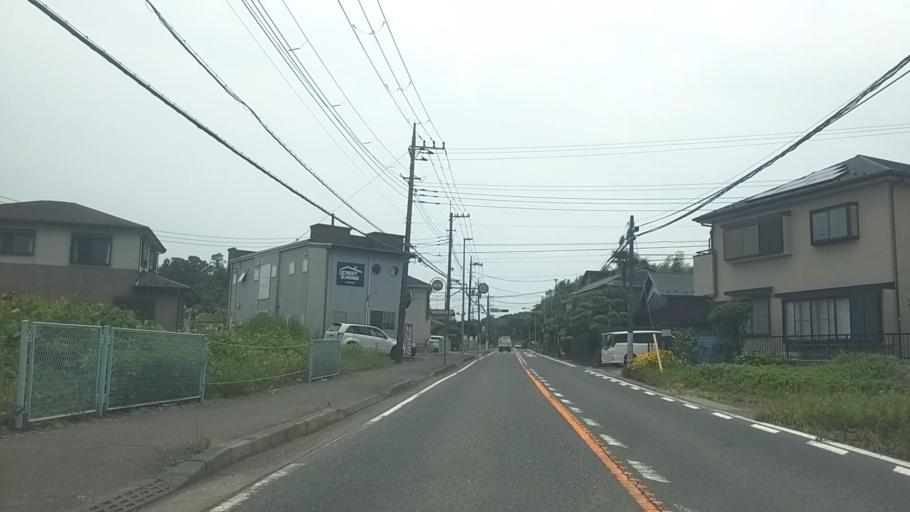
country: JP
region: Kanagawa
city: Chigasaki
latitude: 35.3618
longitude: 139.4219
